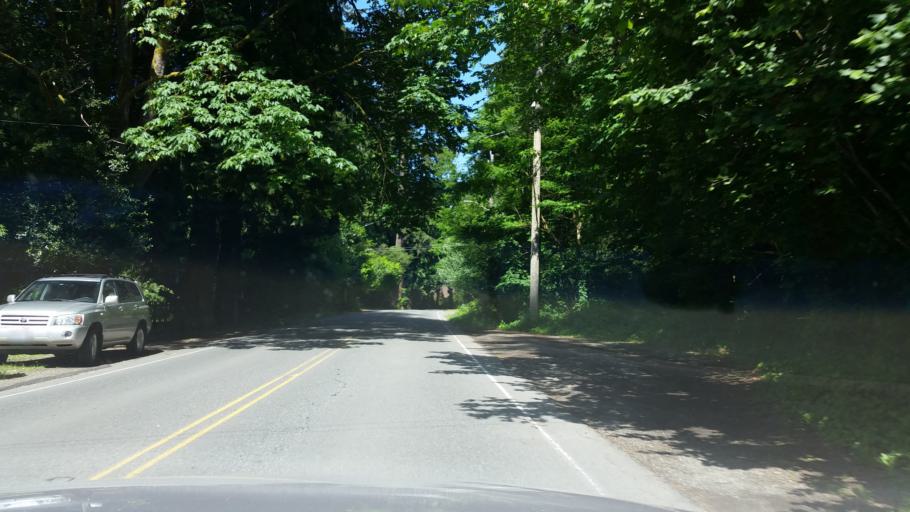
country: US
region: Washington
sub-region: King County
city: Lake Forest Park
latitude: 47.7569
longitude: -122.2888
